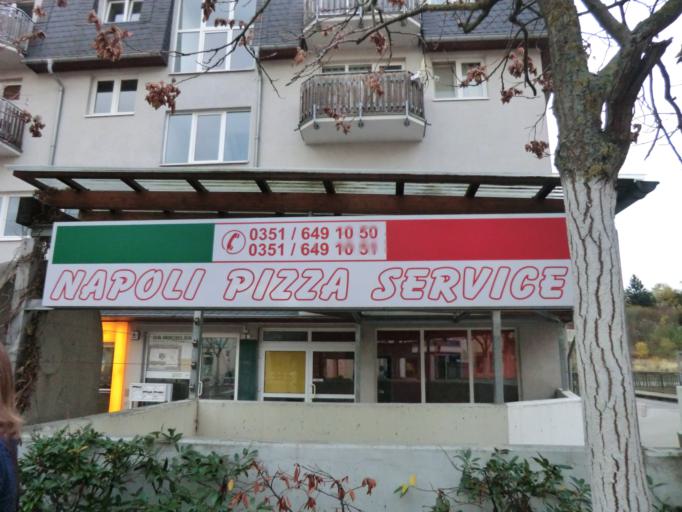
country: DE
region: Saxony
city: Freital
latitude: 51.0114
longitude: 13.6626
